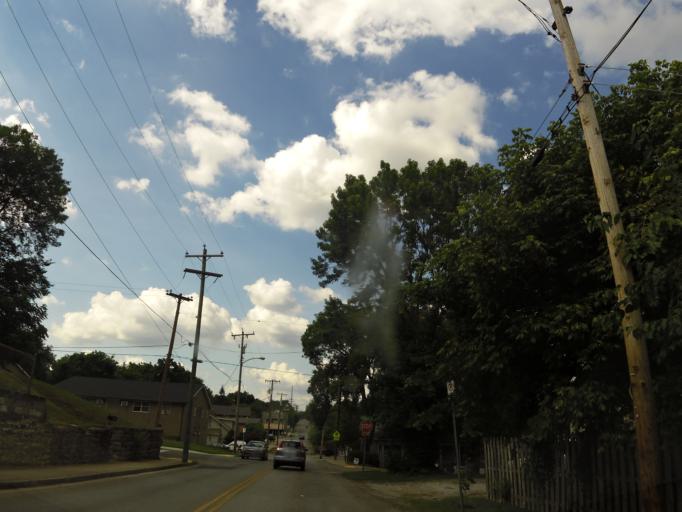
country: US
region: Tennessee
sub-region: Davidson County
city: Nashville
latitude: 36.1754
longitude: -86.7461
